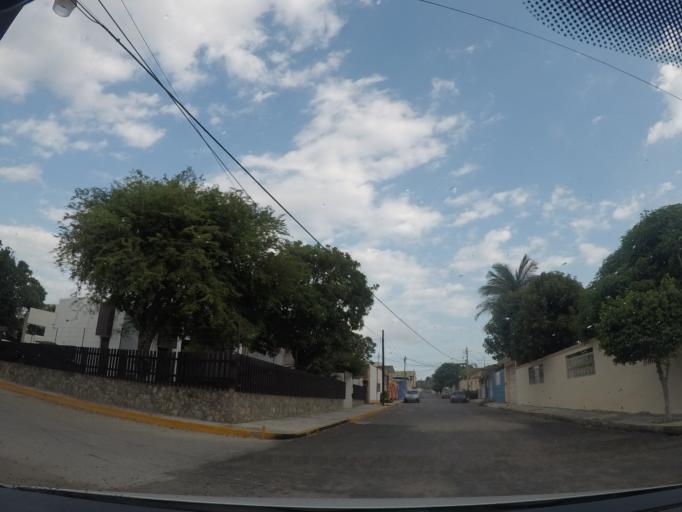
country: MX
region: Oaxaca
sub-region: Salina Cruz
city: Salina Cruz
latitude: 16.2089
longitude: -95.2086
